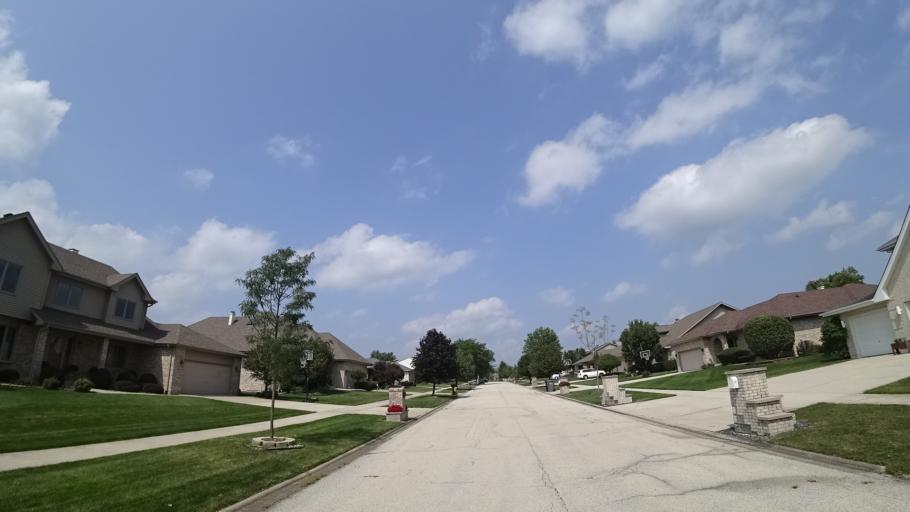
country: US
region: Illinois
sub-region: Will County
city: Goodings Grove
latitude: 41.6338
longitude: -87.9004
